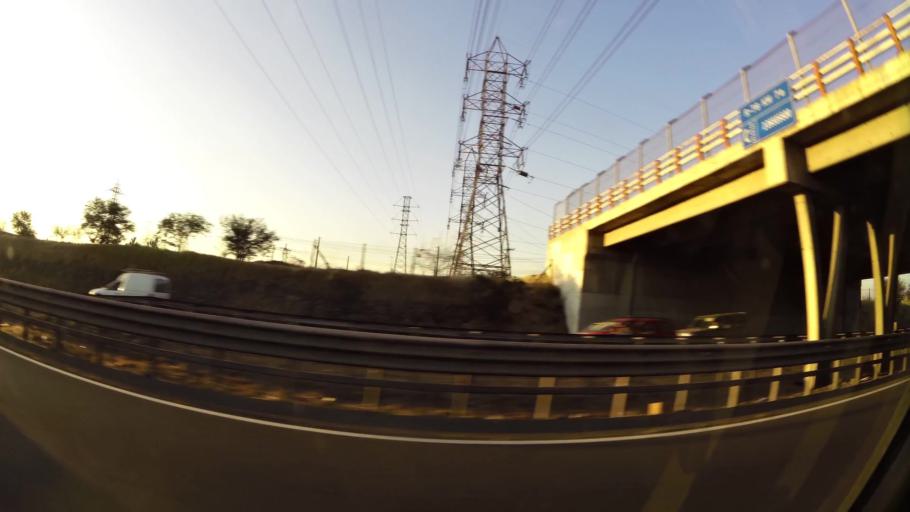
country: CL
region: Santiago Metropolitan
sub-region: Provincia de Santiago
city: Lo Prado
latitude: -33.4842
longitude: -70.7312
